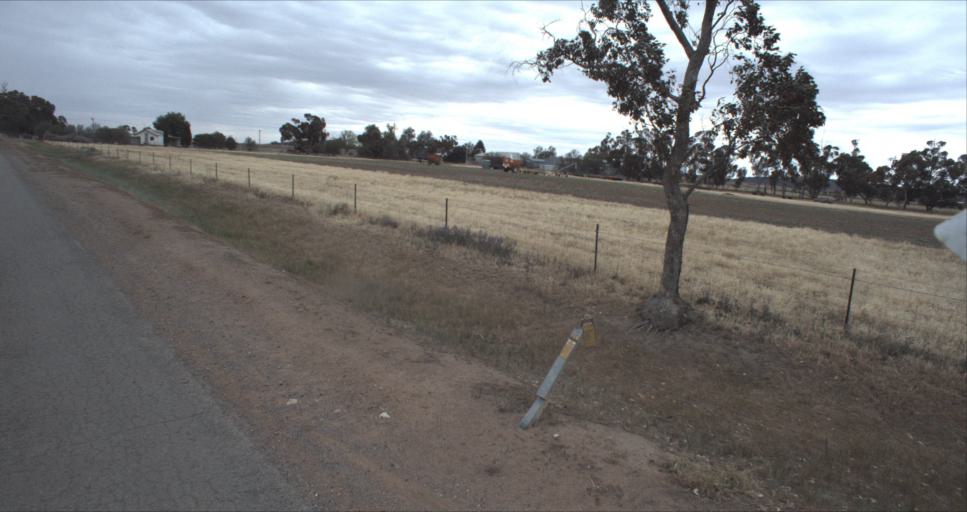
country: AU
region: New South Wales
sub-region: Leeton
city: Leeton
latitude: -34.4082
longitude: 146.3408
